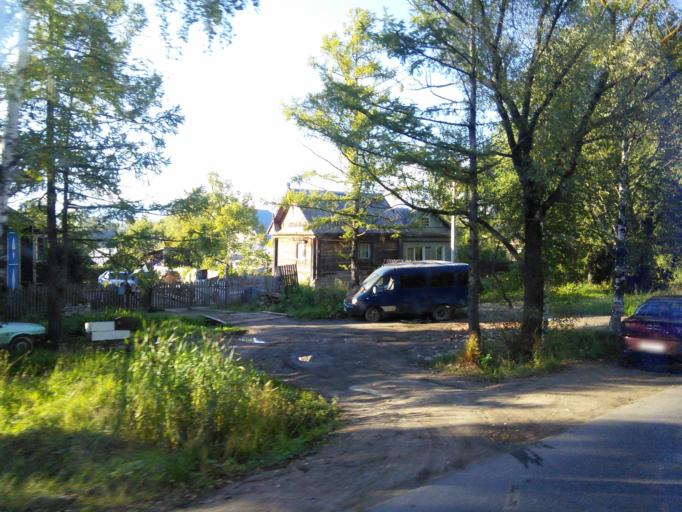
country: RU
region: Jaroslavl
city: Poshekhon'ye
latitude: 58.5008
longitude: 39.1303
